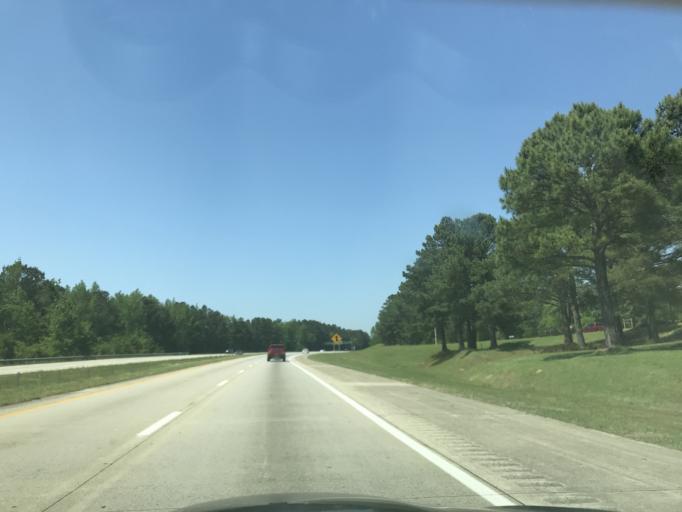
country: US
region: North Carolina
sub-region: Johnston County
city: Benson
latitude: 35.4391
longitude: -78.5340
